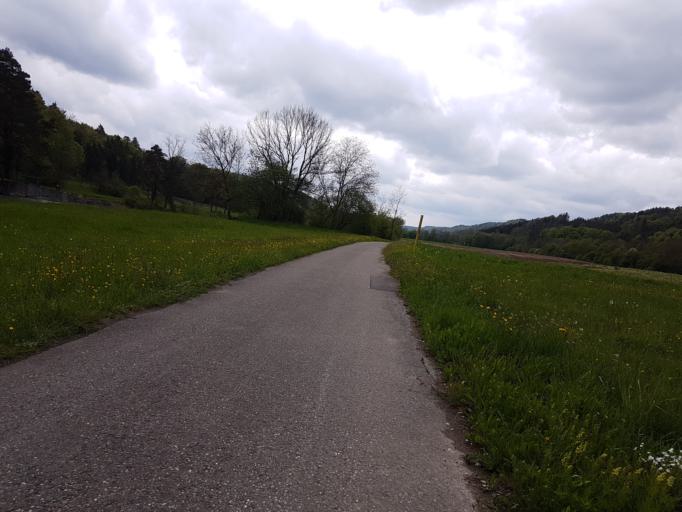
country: DE
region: Baden-Wuerttemberg
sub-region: Freiburg Region
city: Eggingen
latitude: 47.7082
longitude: 8.4150
